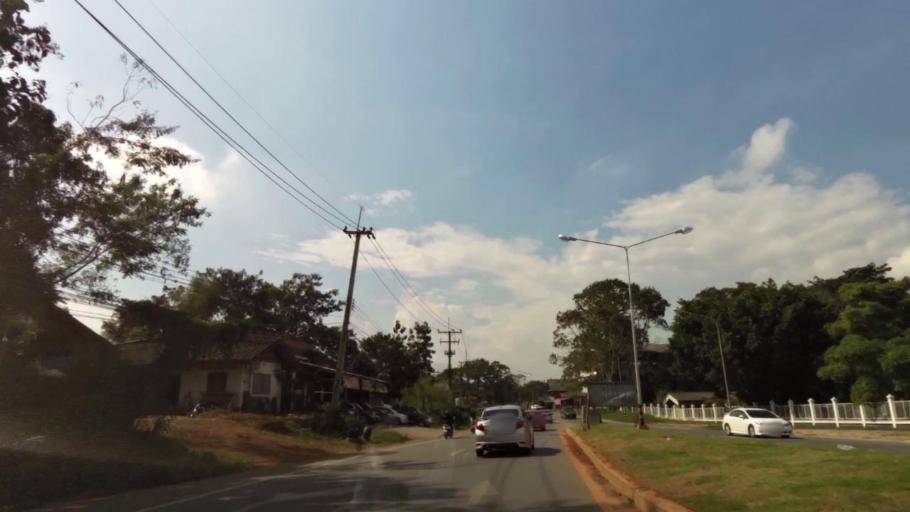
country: TH
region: Chiang Rai
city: Chiang Rai
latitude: 19.8755
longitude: 99.7841
